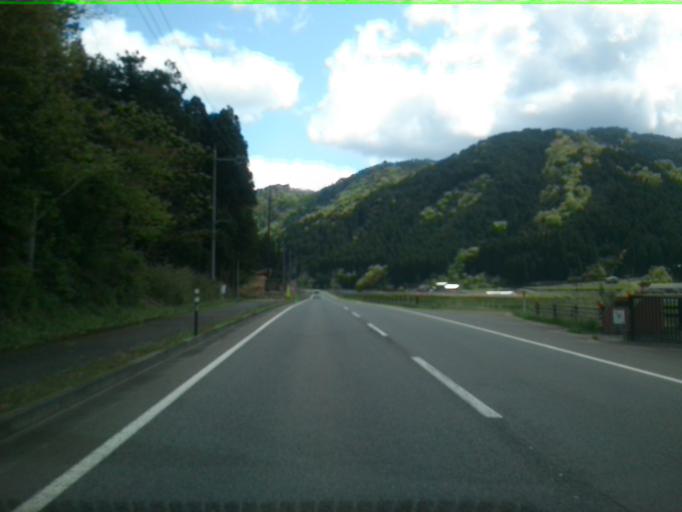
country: JP
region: Kyoto
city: Fukuchiyama
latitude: 35.4353
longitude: 135.0007
